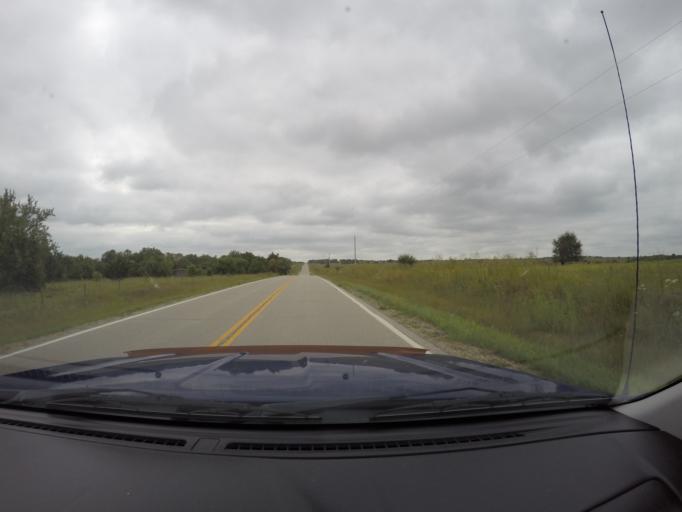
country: US
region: Kansas
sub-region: Morris County
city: Council Grove
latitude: 38.7977
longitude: -96.6805
